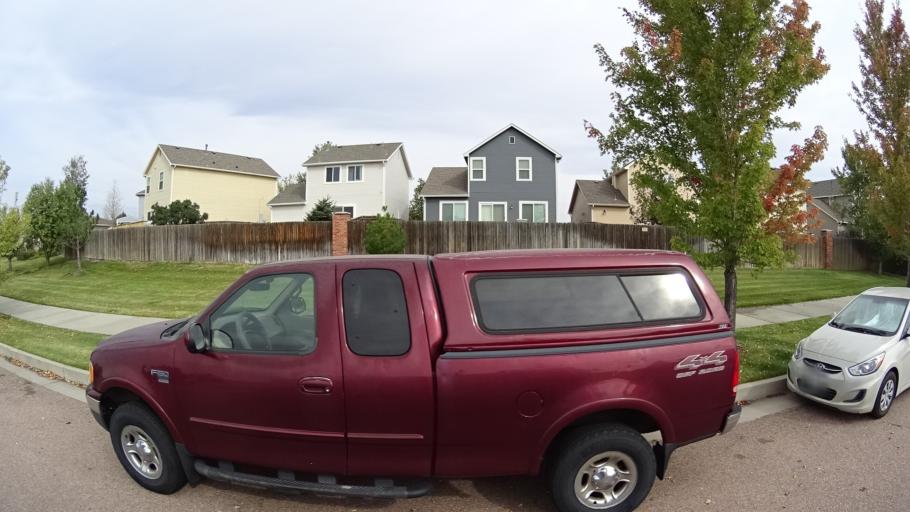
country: US
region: Colorado
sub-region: El Paso County
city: Cimarron Hills
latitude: 38.9195
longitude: -104.7162
